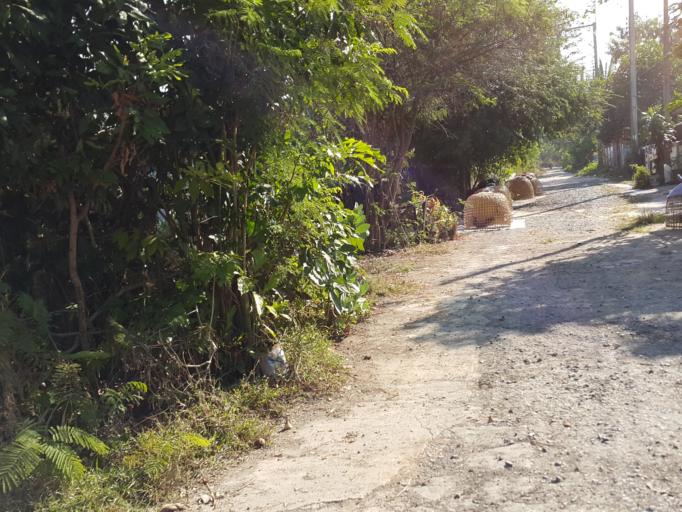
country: TH
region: Chiang Mai
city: San Kamphaeng
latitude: 18.8090
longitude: 99.1106
